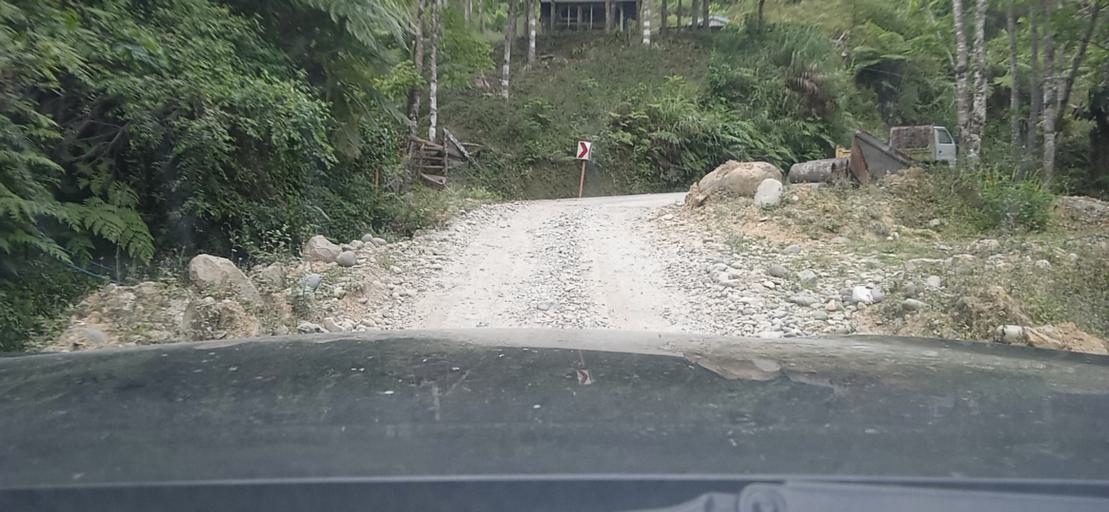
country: PH
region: Cordillera
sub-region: Kalinga
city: Lubuagan
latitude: 17.3737
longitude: 121.1803
